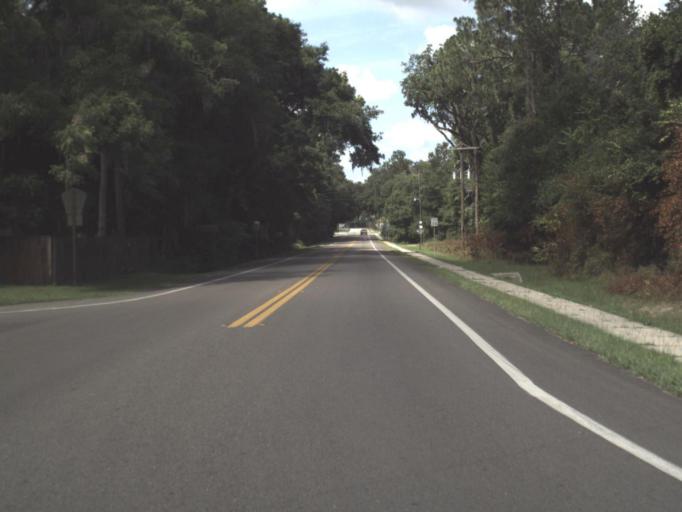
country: US
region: Florida
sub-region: Levy County
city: Bronson
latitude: 29.4500
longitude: -82.6396
